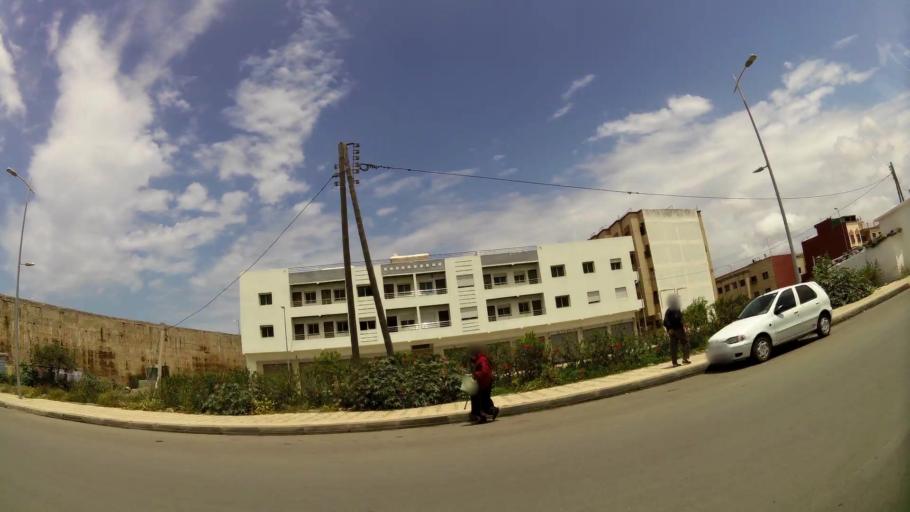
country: MA
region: Rabat-Sale-Zemmour-Zaer
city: Sale
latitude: 34.0444
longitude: -6.8252
